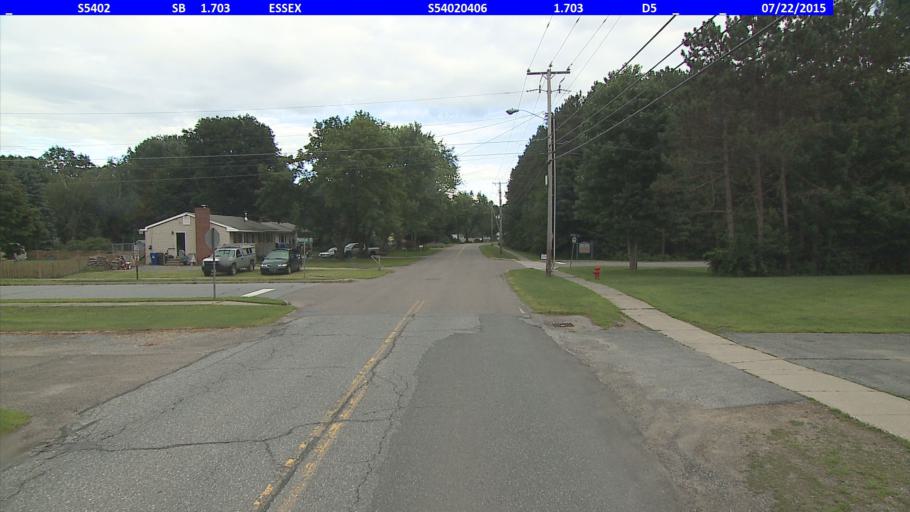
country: US
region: Vermont
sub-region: Chittenden County
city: Jericho
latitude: 44.5024
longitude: -73.0504
